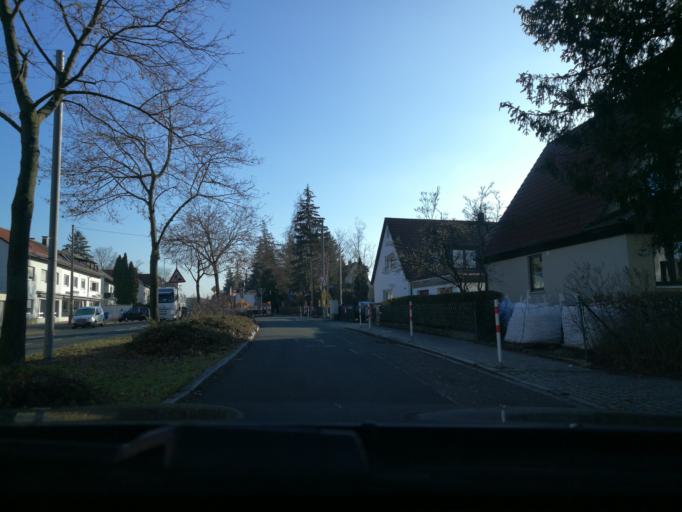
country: DE
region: Bavaria
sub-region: Regierungsbezirk Mittelfranken
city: Buckenhof
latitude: 49.5942
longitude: 11.0439
